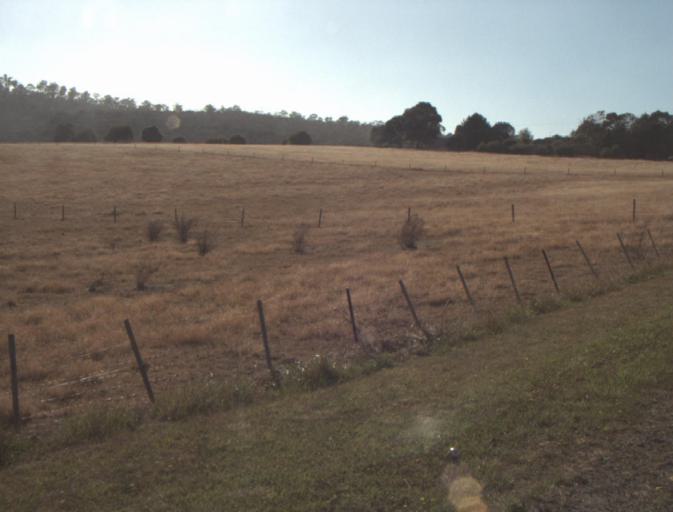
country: AU
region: Tasmania
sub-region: Launceston
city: Newstead
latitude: -41.4392
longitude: 147.2108
